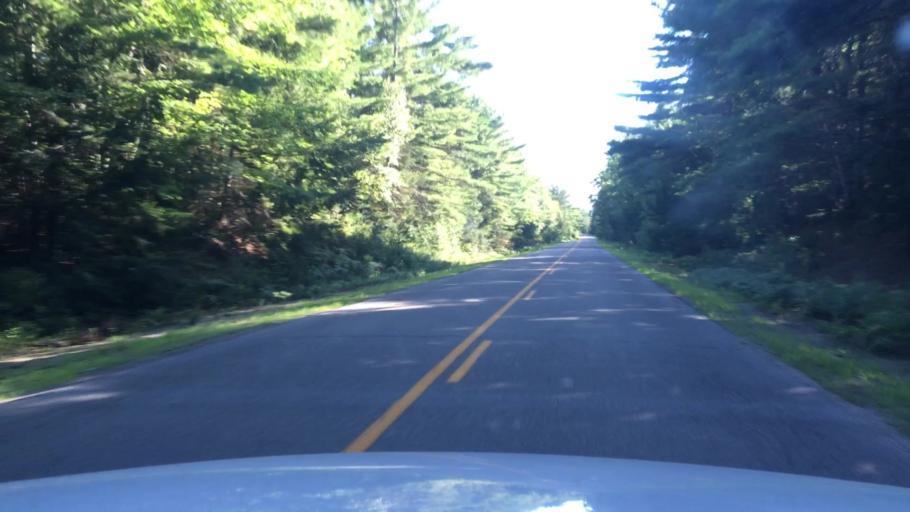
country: US
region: Maine
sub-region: Penobscot County
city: Enfield
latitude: 45.2062
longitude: -68.5936
